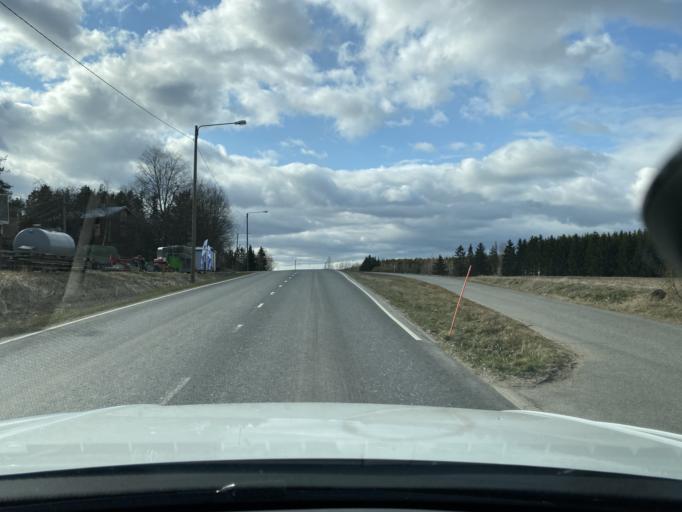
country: FI
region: Pirkanmaa
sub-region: Lounais-Pirkanmaa
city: Punkalaidun
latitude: 61.1200
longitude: 23.0827
